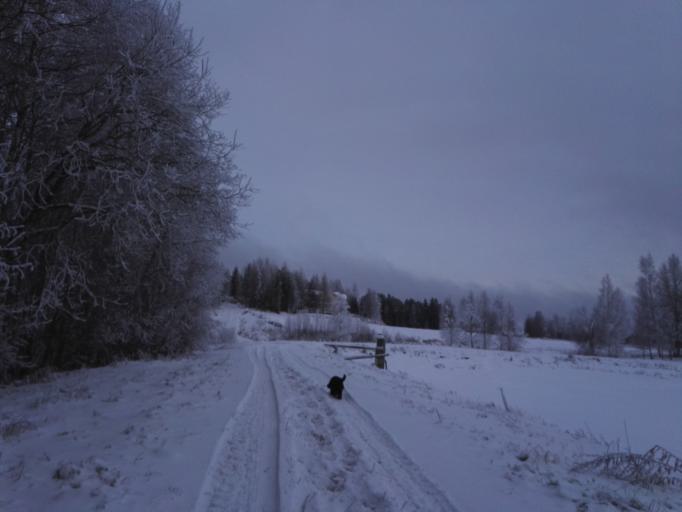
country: FI
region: Satakunta
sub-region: Pohjois-Satakunta
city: Jaemijaervi
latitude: 61.7836
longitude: 22.8768
